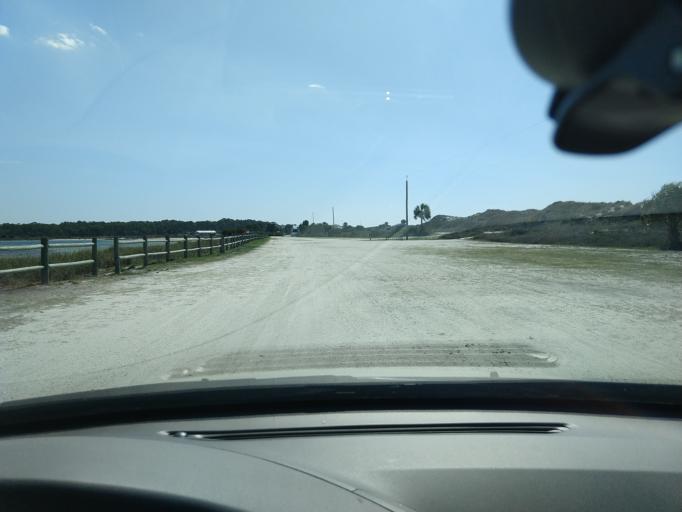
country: US
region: Florida
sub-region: Gulf County
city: Port Saint Joe
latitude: 29.7674
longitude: -85.4044
